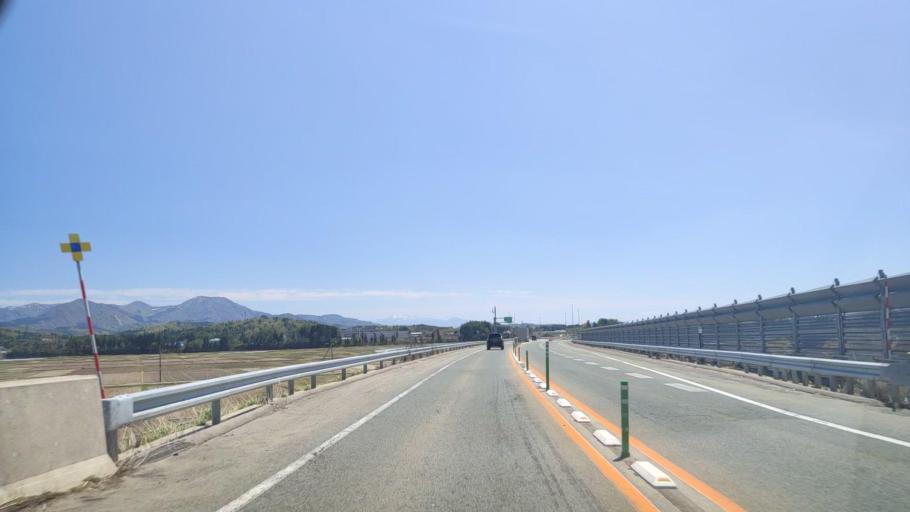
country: JP
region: Yamagata
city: Obanazawa
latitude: 38.6091
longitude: 140.3885
